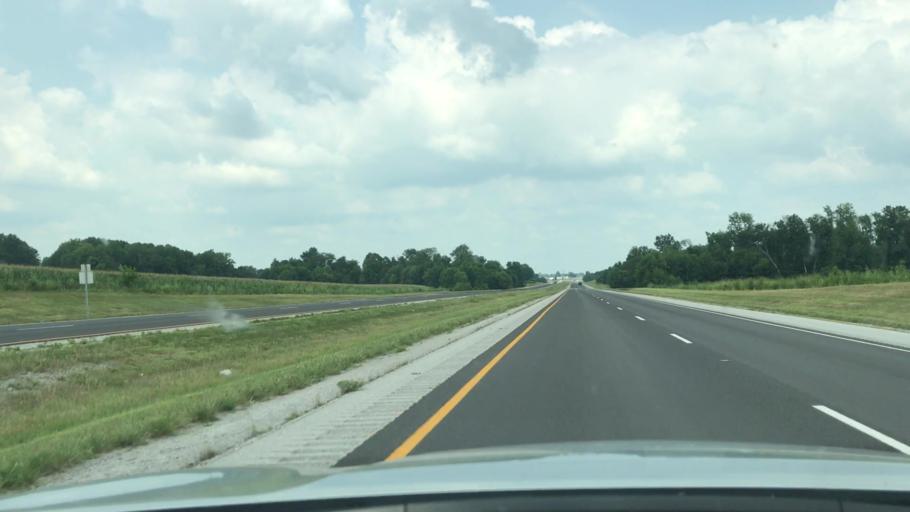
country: US
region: Kentucky
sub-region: Todd County
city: Elkton
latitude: 36.8046
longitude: -87.0690
